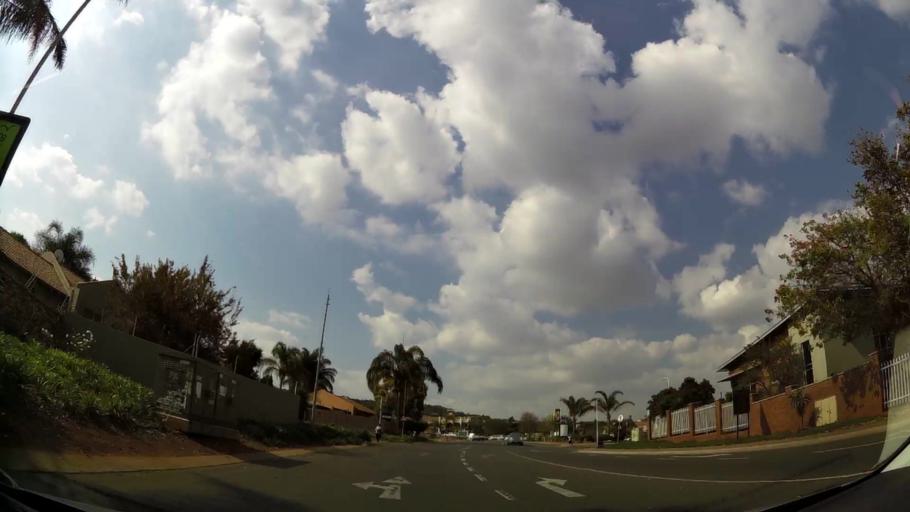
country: ZA
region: Gauteng
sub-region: City of Tshwane Metropolitan Municipality
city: Pretoria
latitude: -25.7890
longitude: 28.3264
